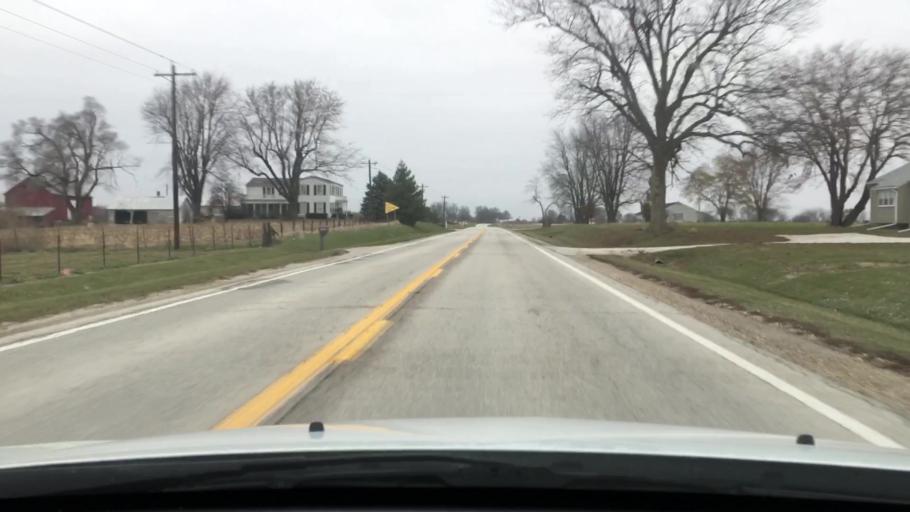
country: US
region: Illinois
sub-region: Pike County
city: Pittsfield
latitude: 39.5558
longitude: -90.9165
